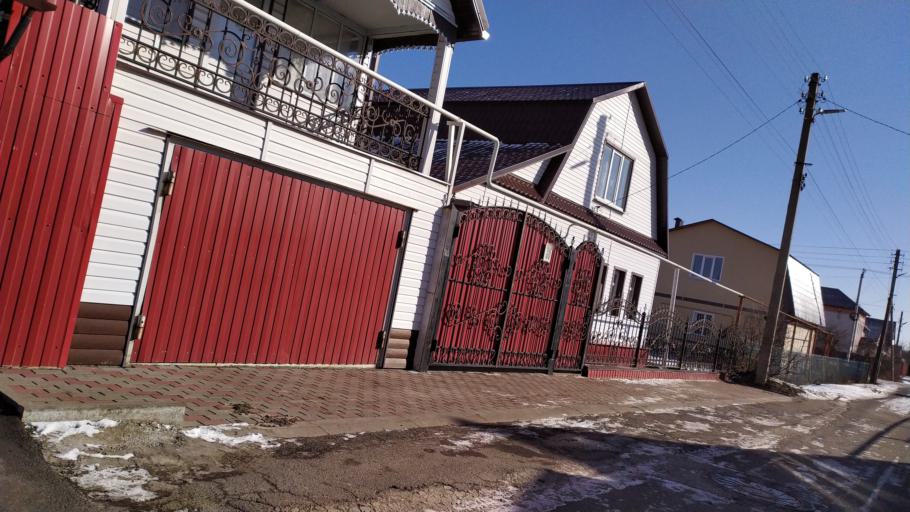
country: RU
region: Kursk
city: Kursk
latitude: 51.6401
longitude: 36.1443
